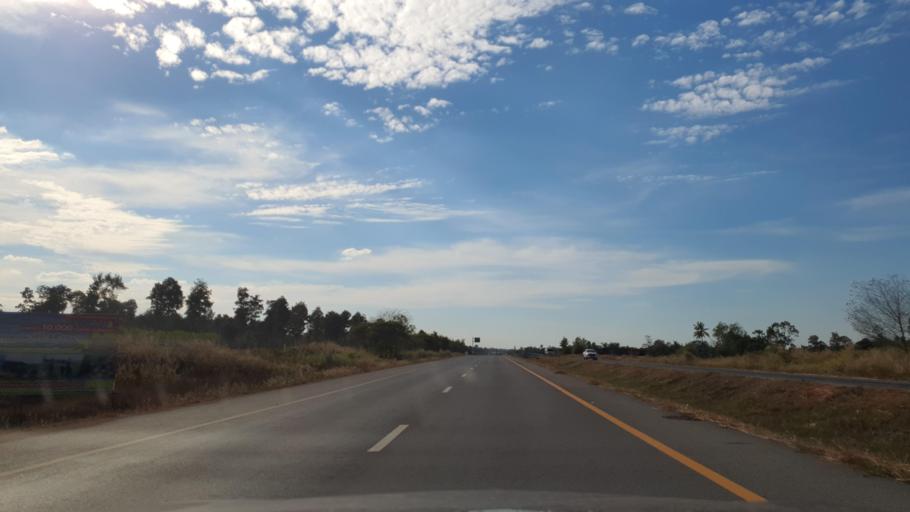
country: TH
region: Roi Et
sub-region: Amphoe Pho Chai
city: Pho Chai
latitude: 16.4126
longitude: 103.7704
